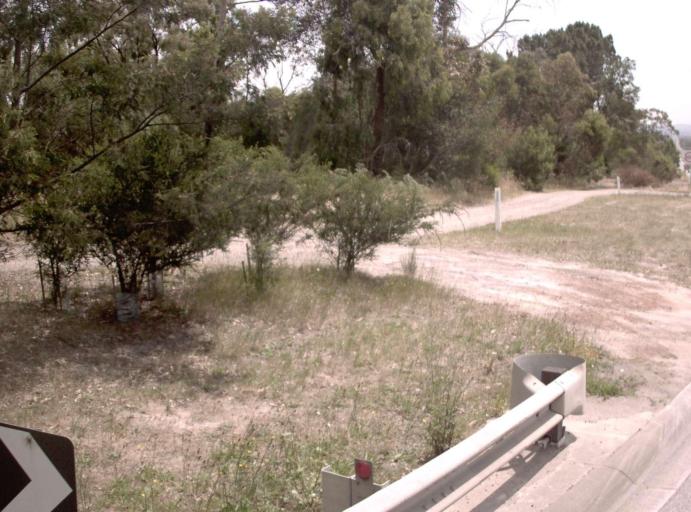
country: AU
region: Victoria
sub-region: Casey
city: Cranbourne South
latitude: -38.1430
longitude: 145.2264
